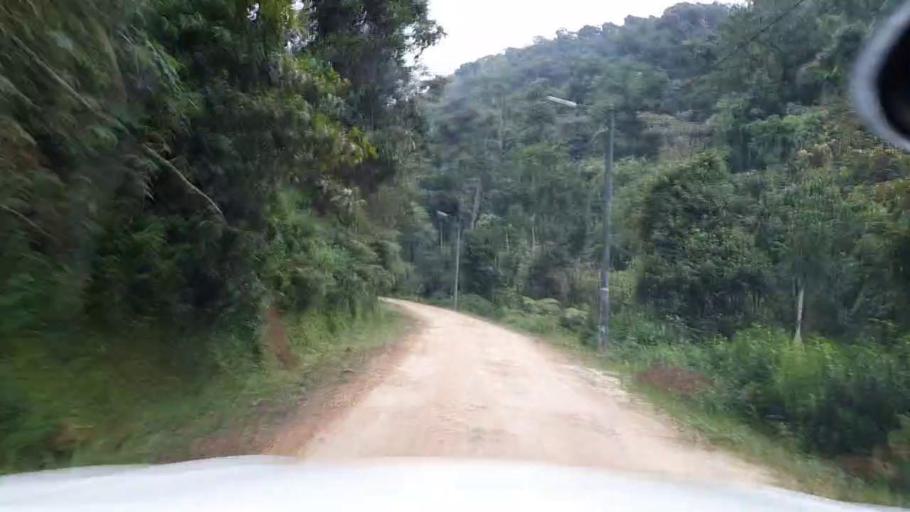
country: RW
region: Western Province
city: Cyangugu
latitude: -2.5705
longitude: 29.2274
